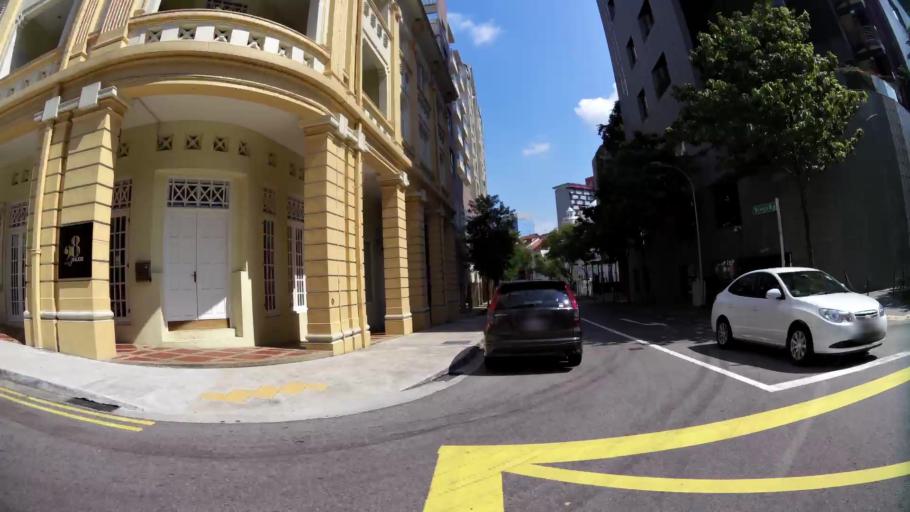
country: SG
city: Singapore
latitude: 1.3021
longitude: 103.8489
